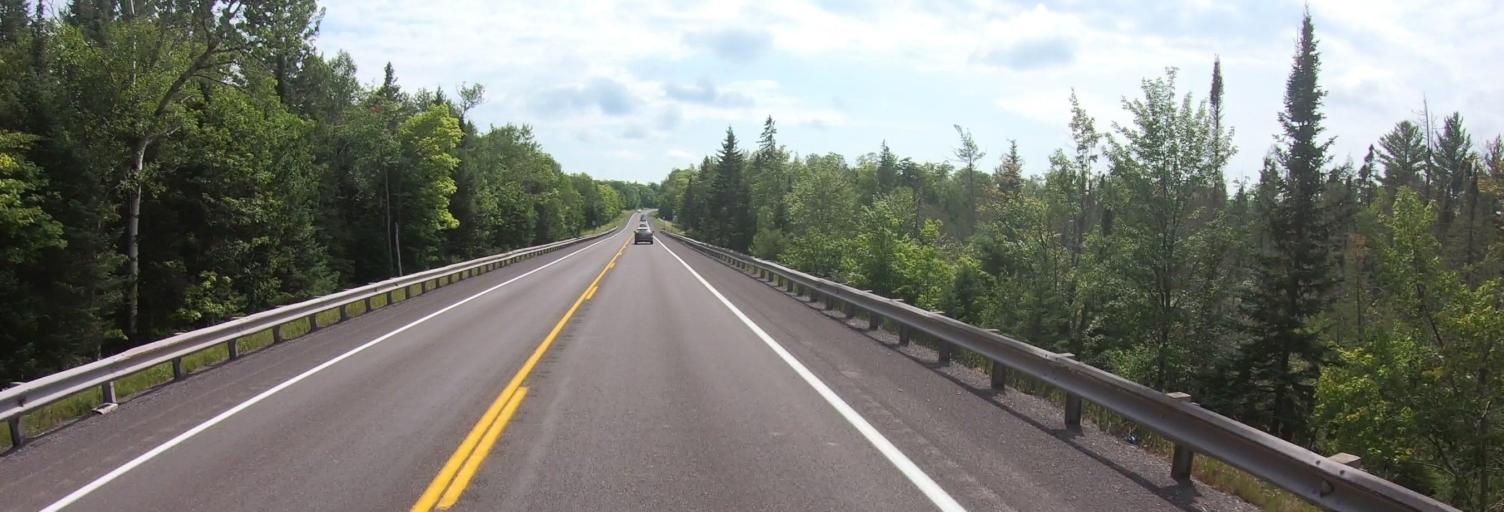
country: US
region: Michigan
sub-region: Houghton County
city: Hancock
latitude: 46.9561
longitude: -88.7798
